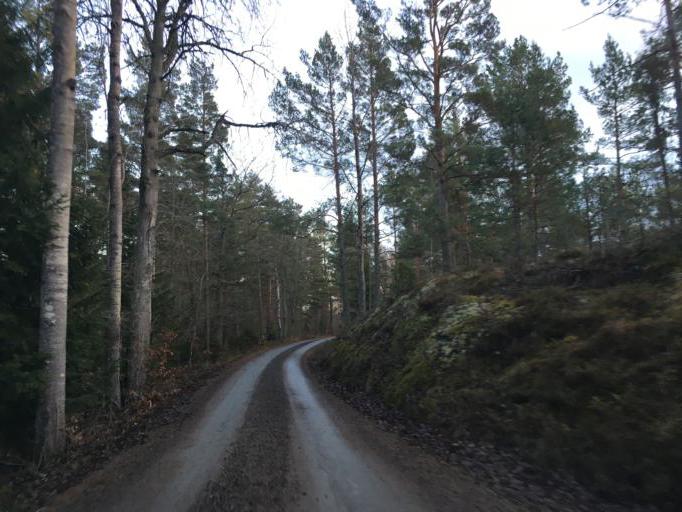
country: SE
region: Kalmar
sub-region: Vasterviks Kommun
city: Vaestervik
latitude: 57.6049
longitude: 16.5301
